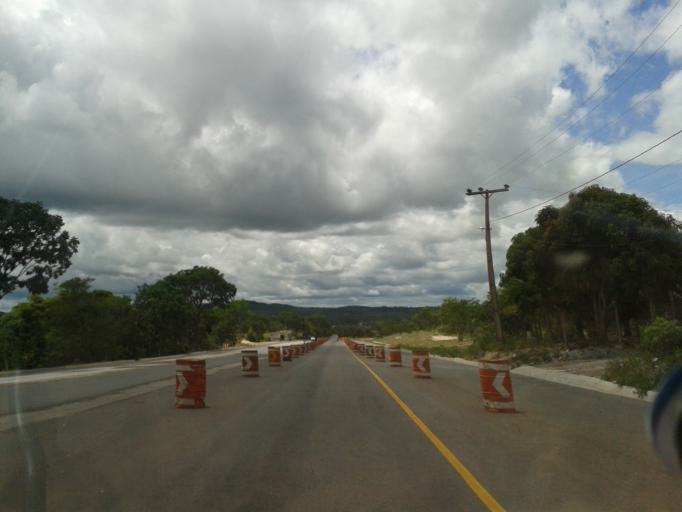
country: BR
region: Goias
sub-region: Goias
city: Goias
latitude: -15.9666
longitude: -50.1161
